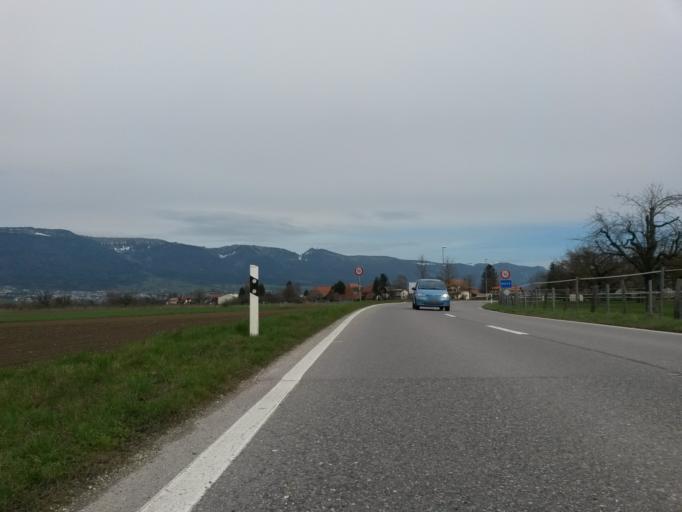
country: CH
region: Bern
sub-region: Seeland District
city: Arch
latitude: 47.1503
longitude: 7.4002
